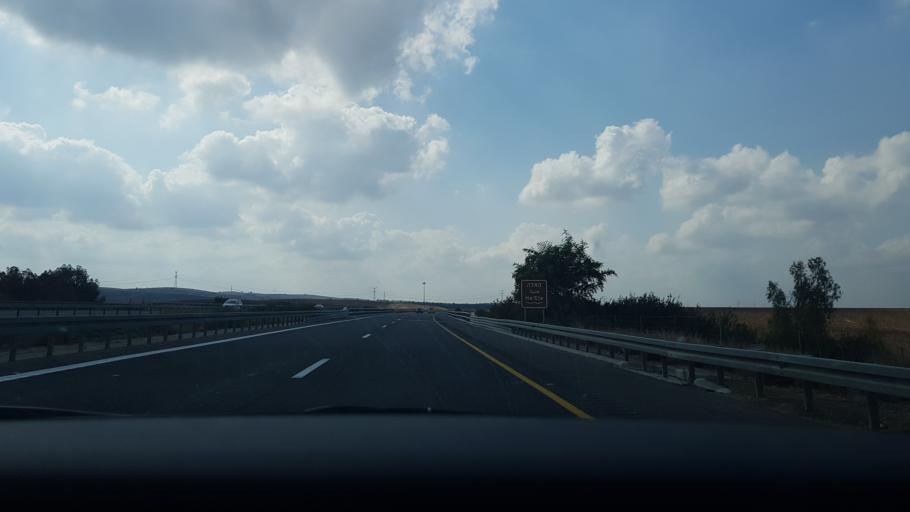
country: IL
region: Central District
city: Bene 'Ayish
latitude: 31.7097
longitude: 34.8202
